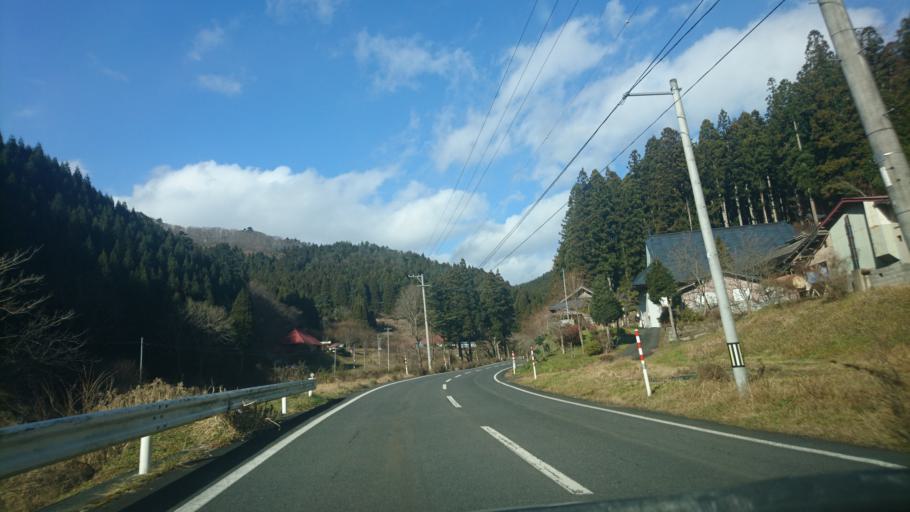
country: JP
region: Iwate
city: Mizusawa
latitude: 39.0911
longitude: 141.3859
